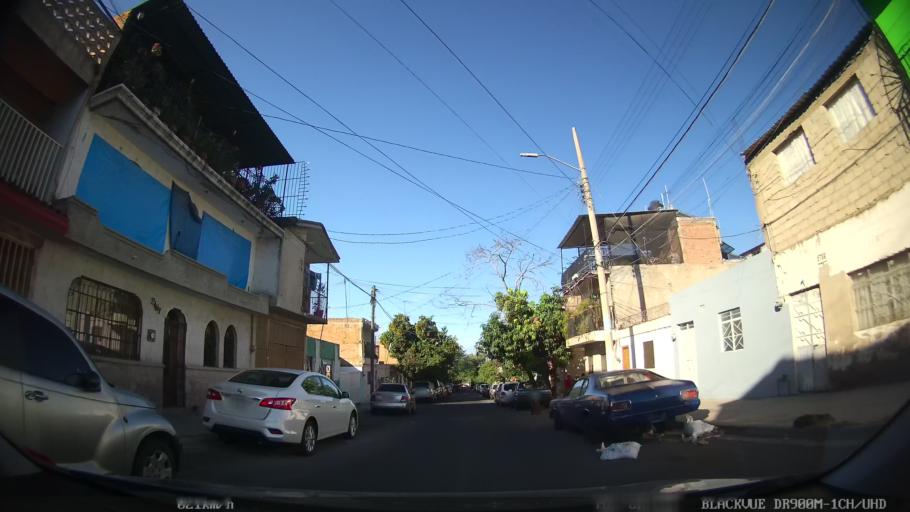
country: MX
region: Jalisco
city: Tlaquepaque
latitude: 20.7055
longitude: -103.2902
